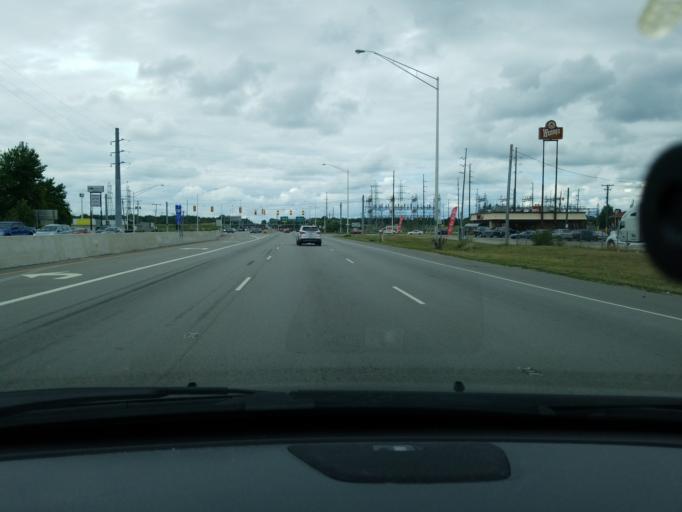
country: US
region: Ohio
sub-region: Lorain County
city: Sheffield
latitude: 41.3988
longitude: -82.1165
